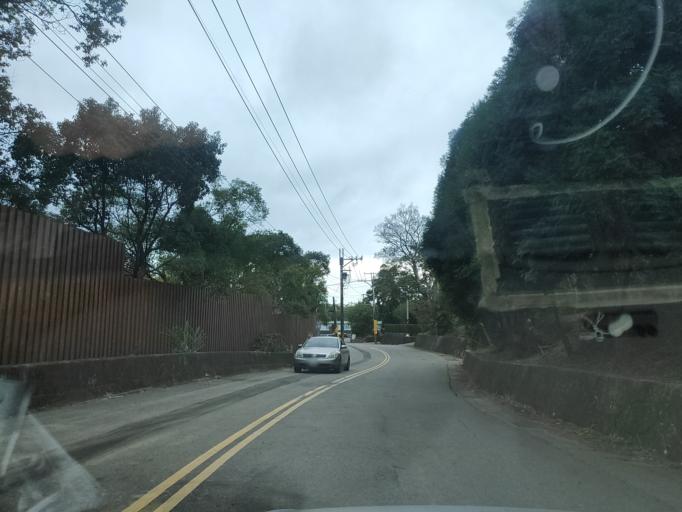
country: TW
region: Taiwan
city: Fengyuan
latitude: 24.3792
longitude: 120.7590
